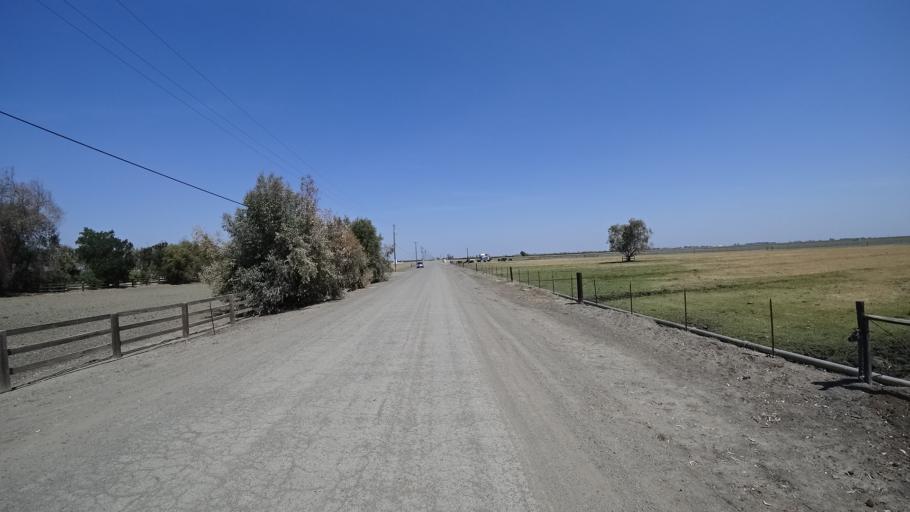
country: US
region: California
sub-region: Kings County
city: Stratford
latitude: 36.1568
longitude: -119.8517
